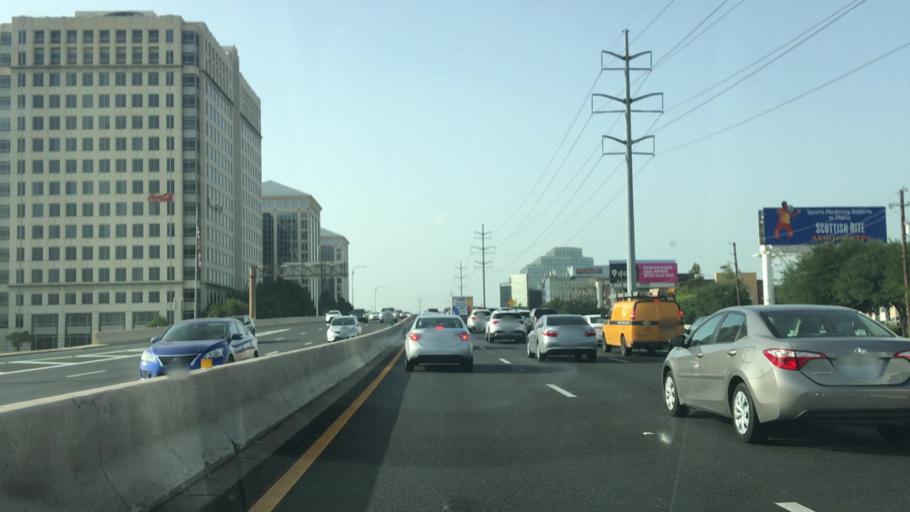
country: US
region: Texas
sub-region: Dallas County
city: Addison
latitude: 32.9373
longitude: -96.8220
